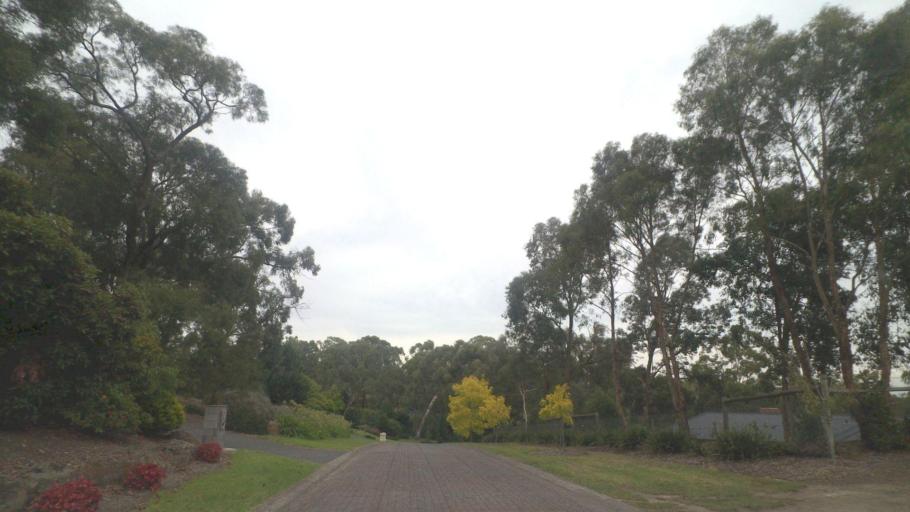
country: AU
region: Victoria
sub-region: Manningham
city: Park Orchards
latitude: -37.7528
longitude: 145.1878
